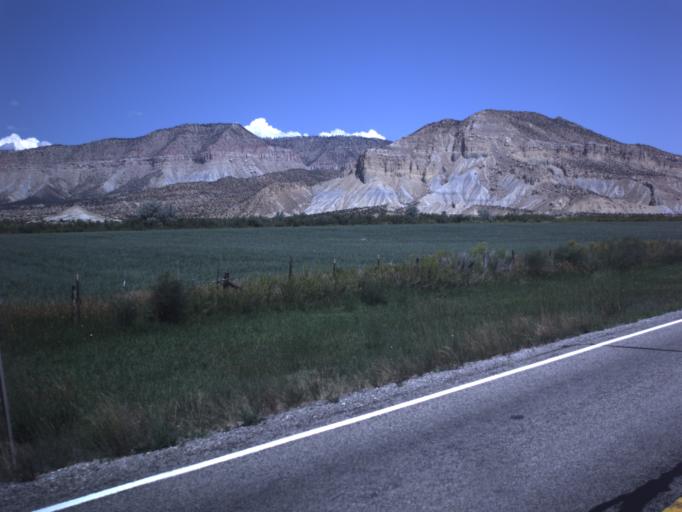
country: US
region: Utah
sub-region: Emery County
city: Ferron
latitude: 38.9038
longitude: -111.2725
